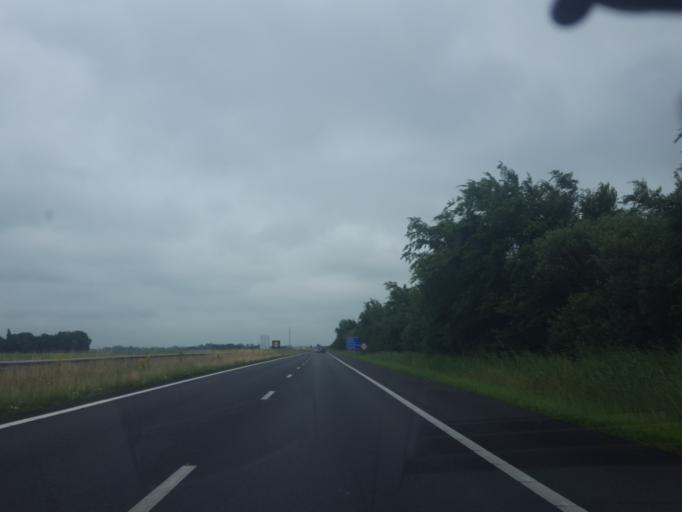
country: NL
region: Friesland
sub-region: Gemeente Leeuwarden
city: Wirdum
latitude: 53.1393
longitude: 5.7985
